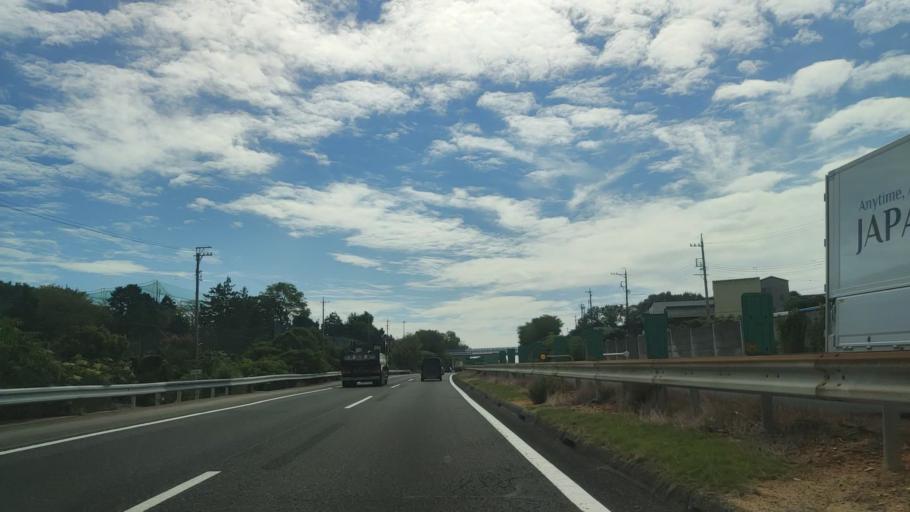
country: JP
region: Aichi
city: Okazaki
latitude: 34.9866
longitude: 137.1853
